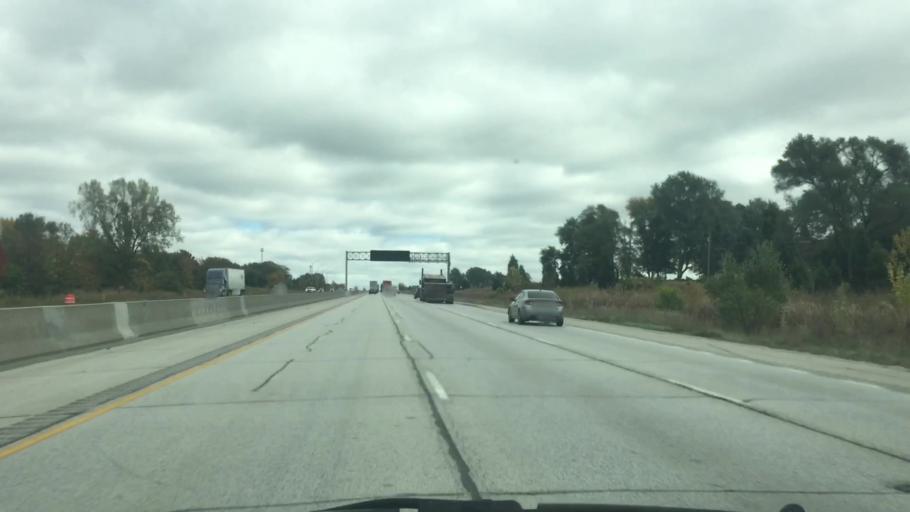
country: US
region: Iowa
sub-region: Polk County
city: Altoona
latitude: 41.6574
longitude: -93.5393
